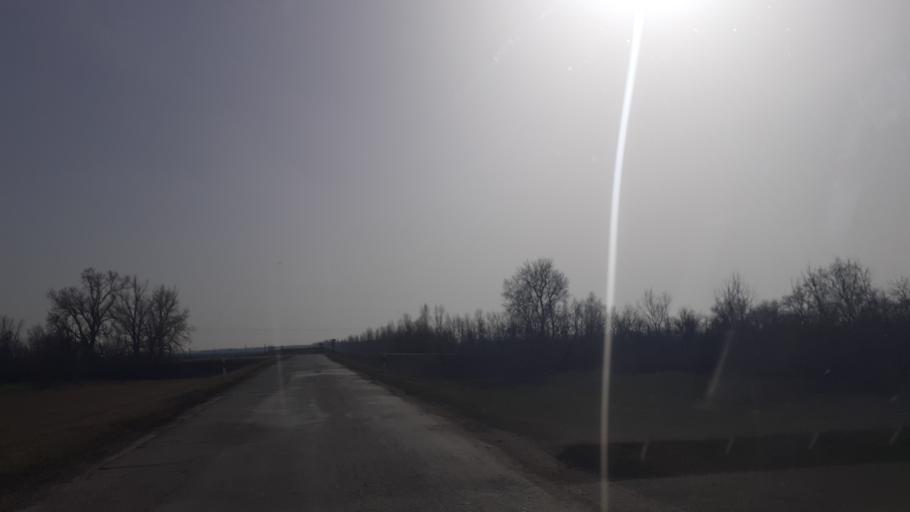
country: HU
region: Fejer
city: Racalmas
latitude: 47.0244
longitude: 18.9830
